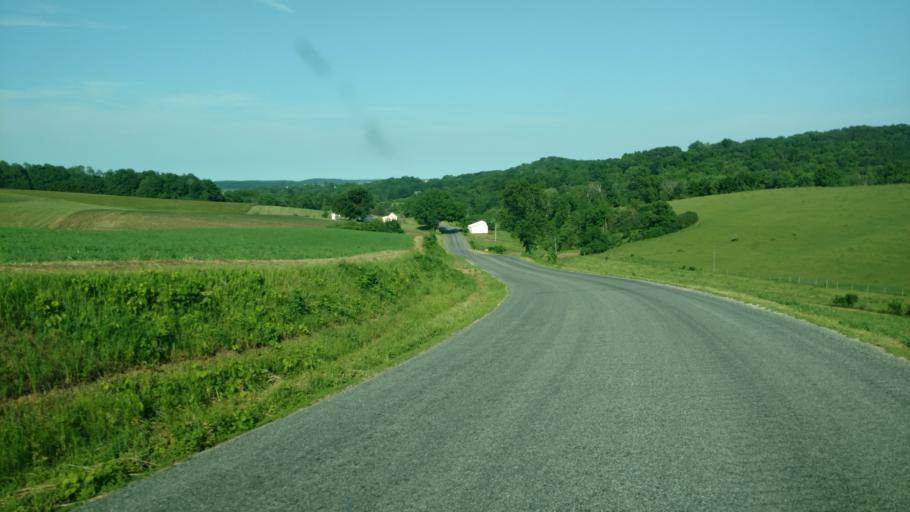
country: US
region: Wisconsin
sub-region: Vernon County
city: Hillsboro
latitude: 43.6814
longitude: -90.3676
